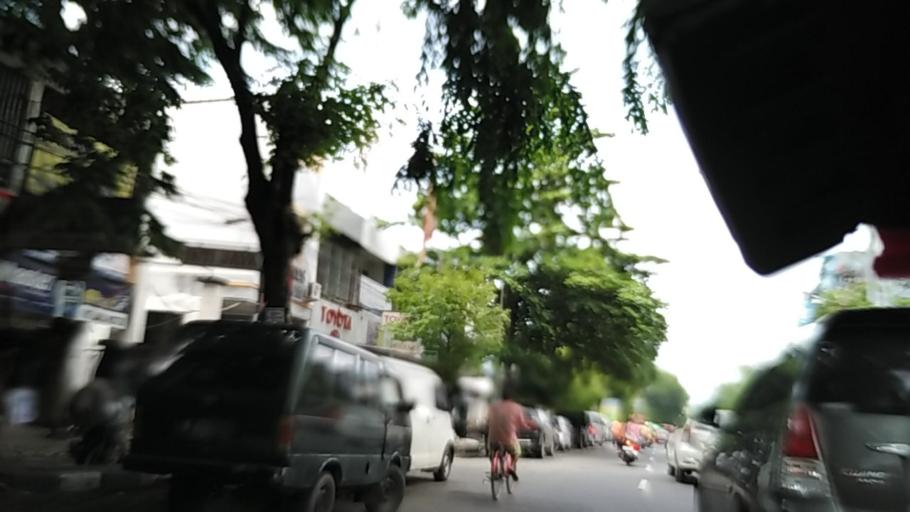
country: ID
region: Central Java
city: Semarang
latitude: -6.9767
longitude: 110.4312
